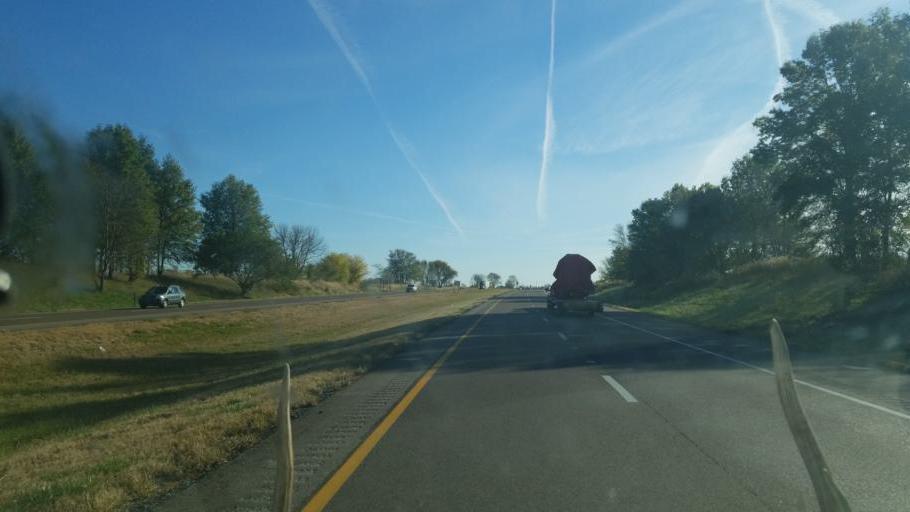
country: US
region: Illinois
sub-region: Madison County
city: Troy
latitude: 38.7624
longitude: -89.8206
